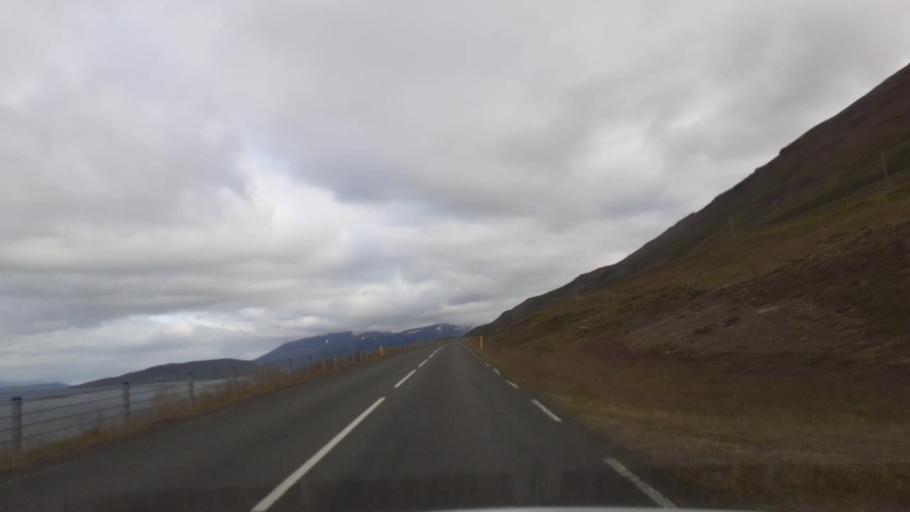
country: IS
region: Northeast
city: Akureyri
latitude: 65.8459
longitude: -18.0588
